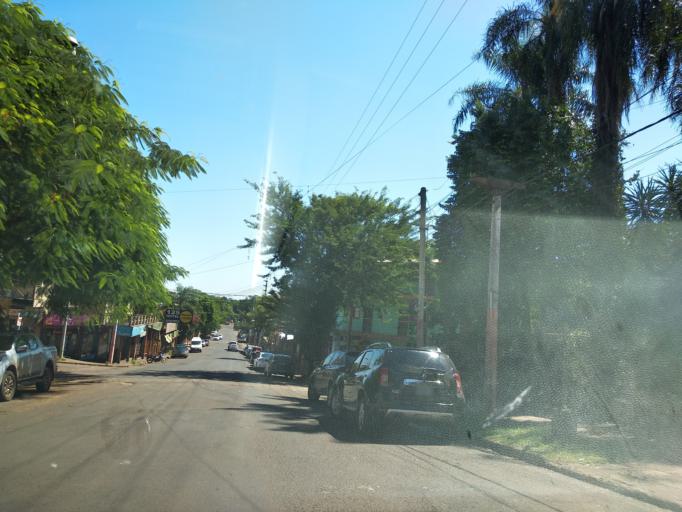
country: AR
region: Misiones
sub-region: Departamento de Iguazu
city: Puerto Iguazu
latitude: -25.5977
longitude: -54.5718
